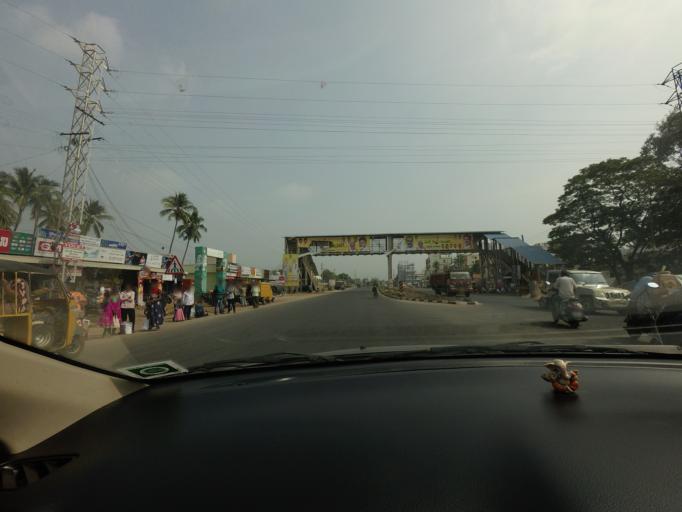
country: IN
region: Andhra Pradesh
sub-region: Krishna
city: Yanamalakuduru
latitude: 16.4713
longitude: 80.7203
